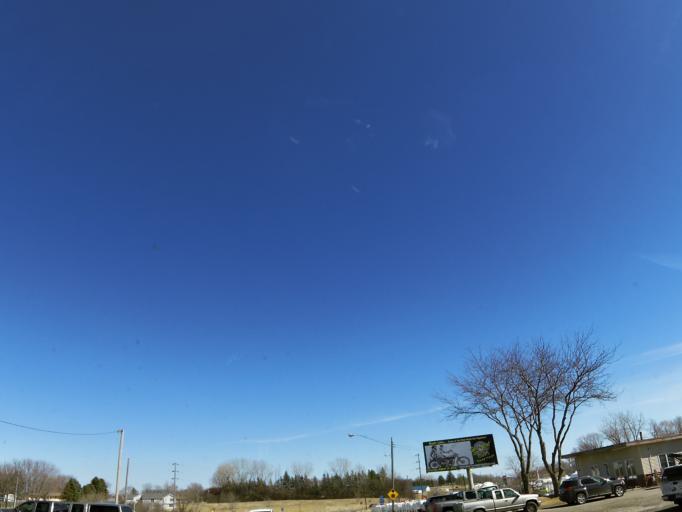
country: US
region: Minnesota
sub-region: Wright County
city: Maple Lake
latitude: 45.2295
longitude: -93.9934
